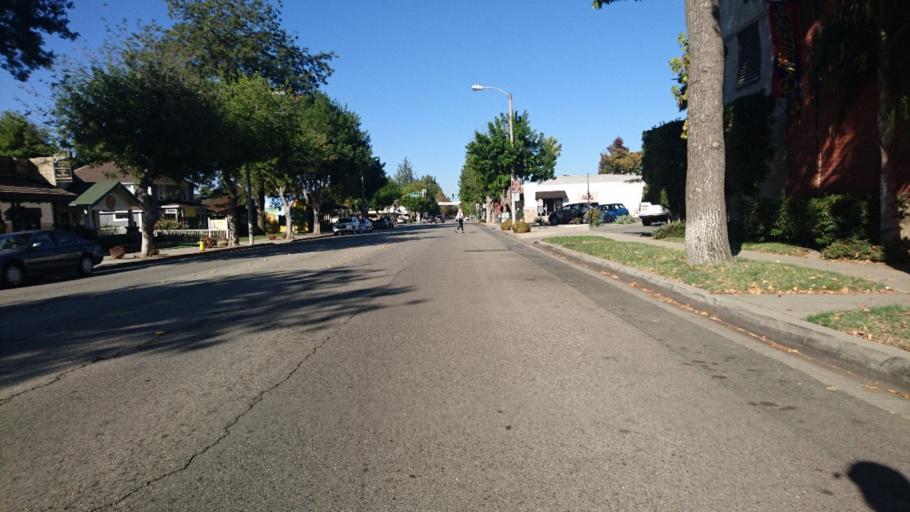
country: US
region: California
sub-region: Los Angeles County
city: La Verne
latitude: 34.1012
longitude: -117.7684
